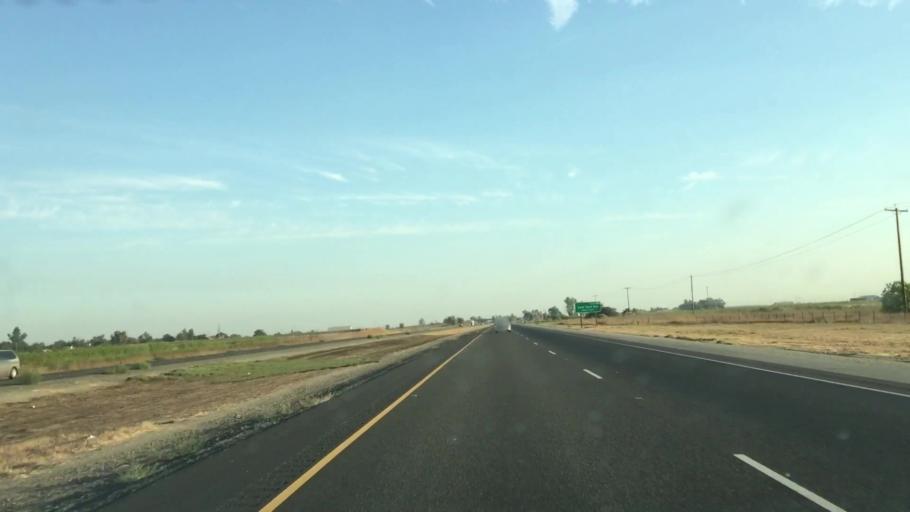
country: US
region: California
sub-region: Colusa County
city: Maxwell
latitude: 39.2634
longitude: -122.1822
